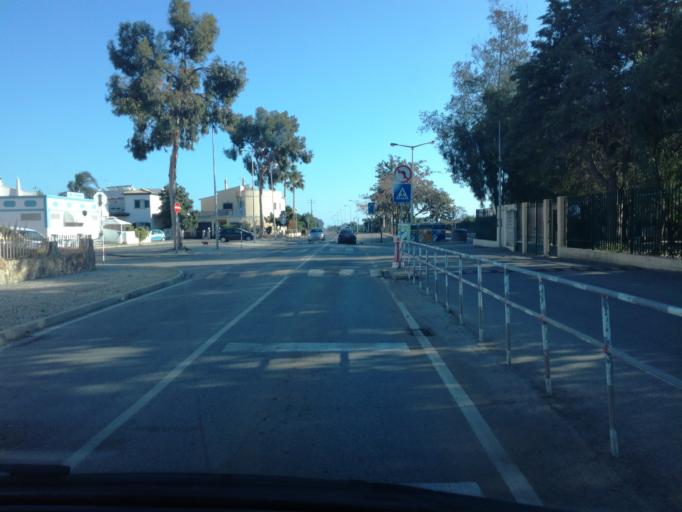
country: PT
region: Faro
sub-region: Olhao
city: Laranjeiro
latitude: 37.0574
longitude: -7.7620
